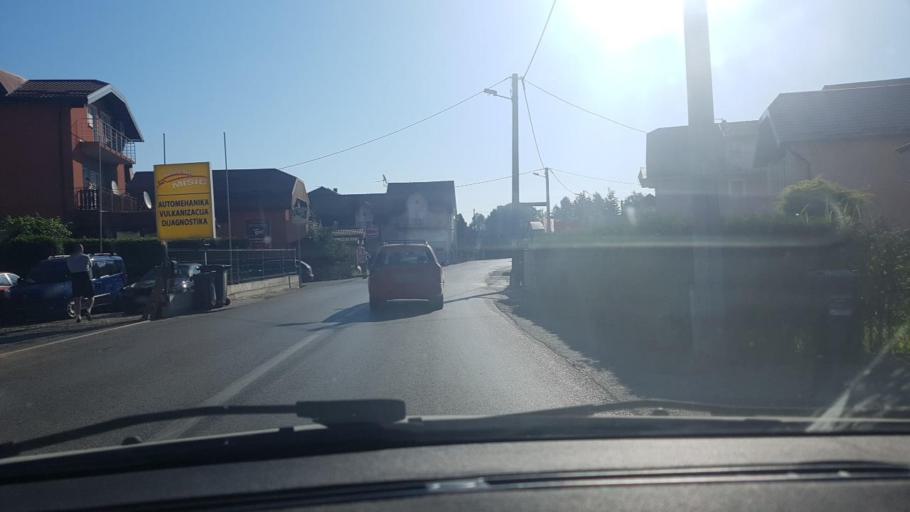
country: HR
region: Grad Zagreb
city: Novi Zagreb
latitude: 45.7655
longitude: 15.9614
